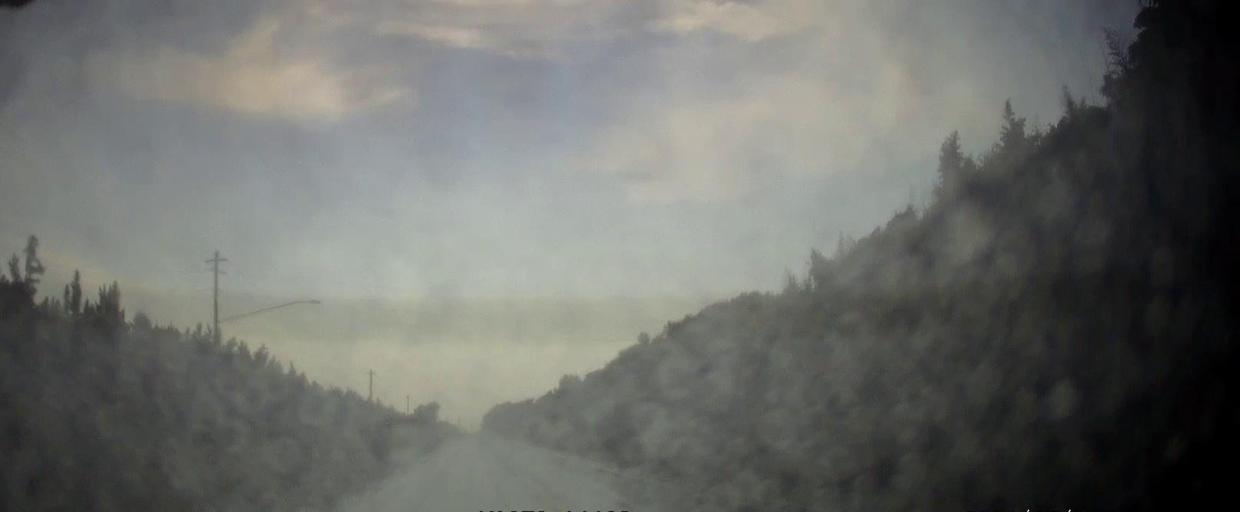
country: US
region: Georgia
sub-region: Dodge County
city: Chester
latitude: 32.5612
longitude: -83.1583
